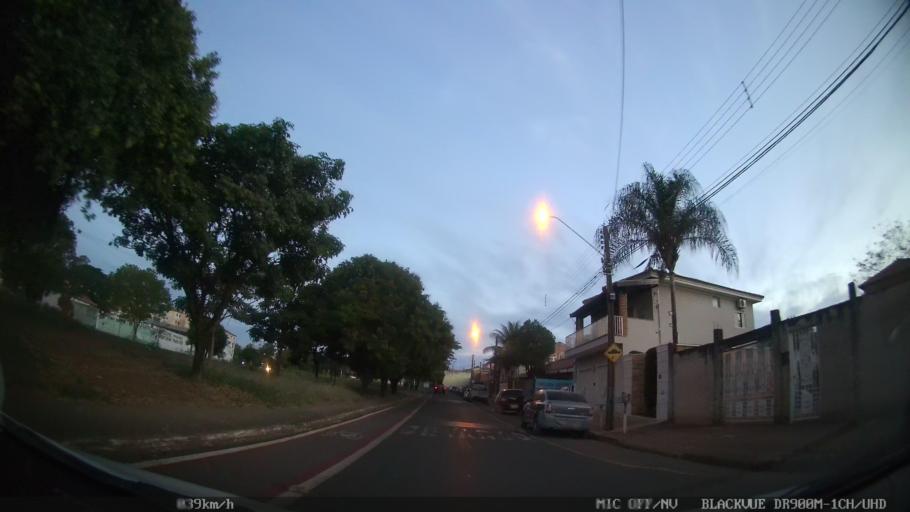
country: BR
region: Sao Paulo
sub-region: Catanduva
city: Catanduva
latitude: -21.1355
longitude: -48.9898
